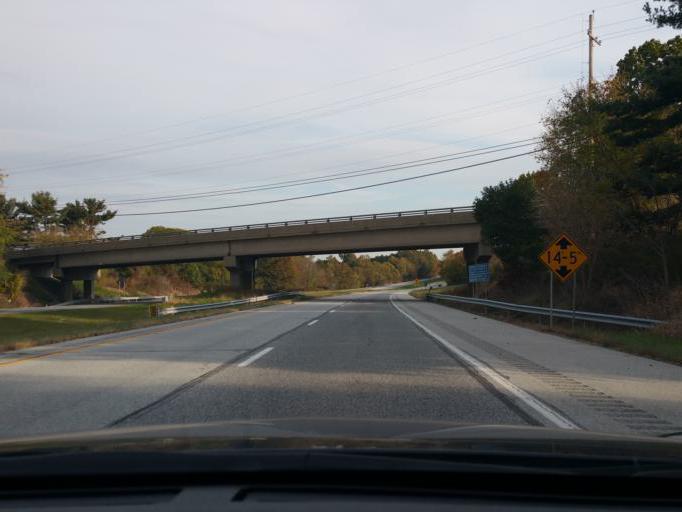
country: US
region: Pennsylvania
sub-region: Chester County
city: Oxford
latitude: 39.7502
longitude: -76.0240
